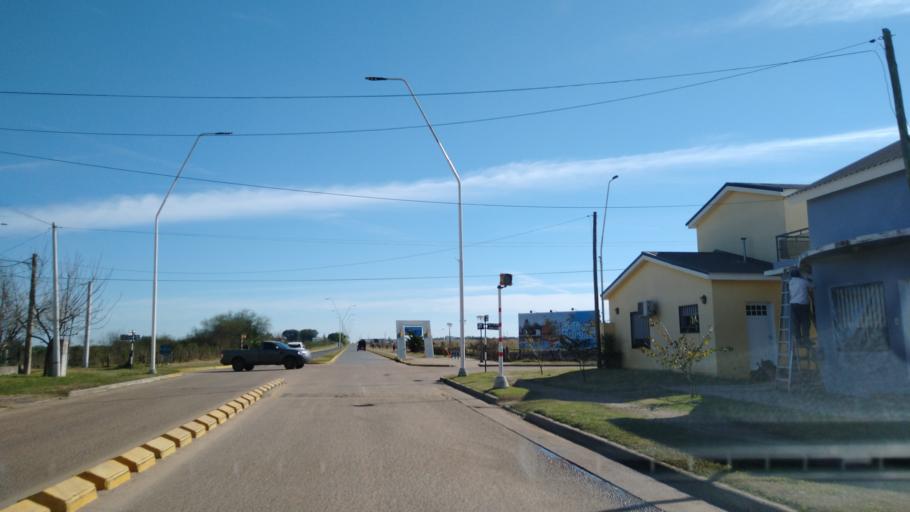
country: AR
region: Entre Rios
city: Chajari
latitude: -30.7589
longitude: -57.9992
